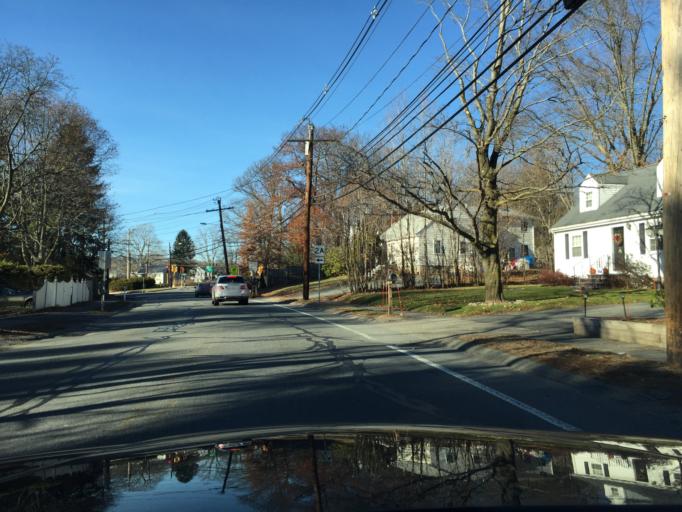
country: US
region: Massachusetts
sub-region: Middlesex County
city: Lexington
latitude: 42.4439
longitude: -71.1953
